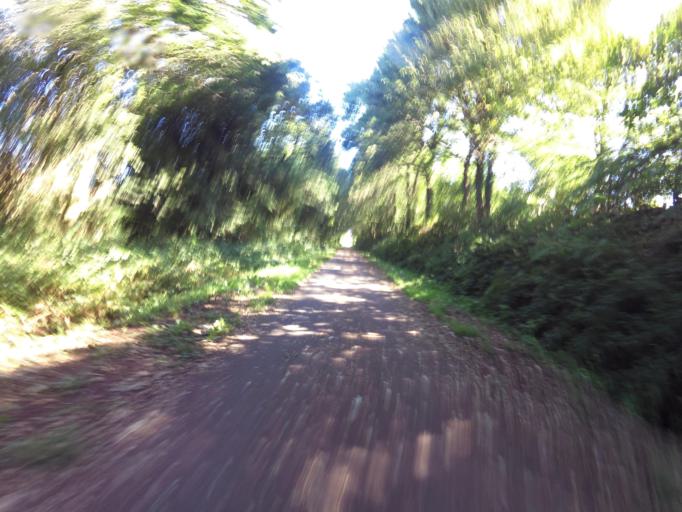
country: FR
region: Brittany
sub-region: Departement du Morbihan
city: Guillac
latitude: 47.8817
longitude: -2.4368
